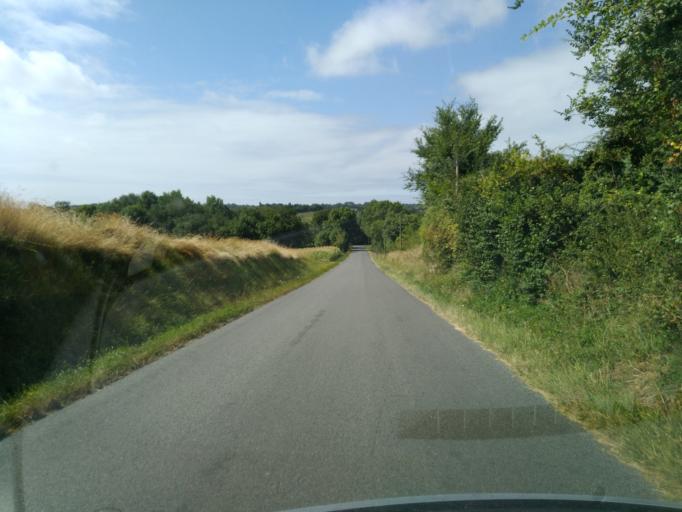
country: FR
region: Poitou-Charentes
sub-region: Departement de la Charente-Maritime
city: Breuillet
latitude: 45.6847
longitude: -1.0783
